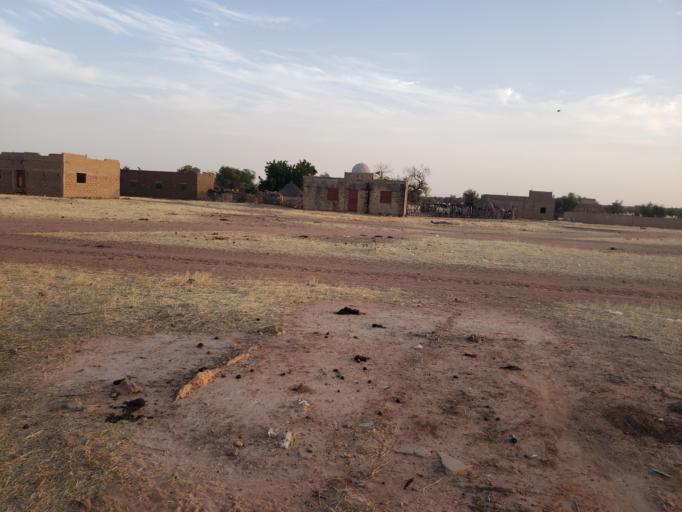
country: SN
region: Matam
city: Ranerou
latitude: 15.2979
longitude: -13.9668
